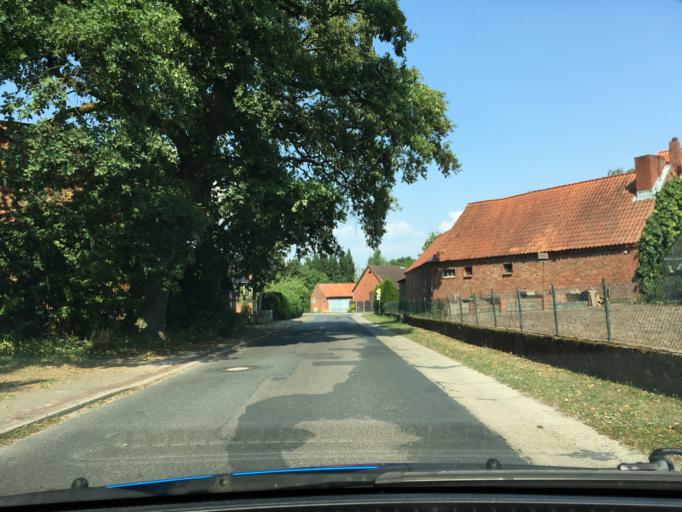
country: DE
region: Lower Saxony
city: Tosterglope
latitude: 53.2429
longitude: 10.7799
